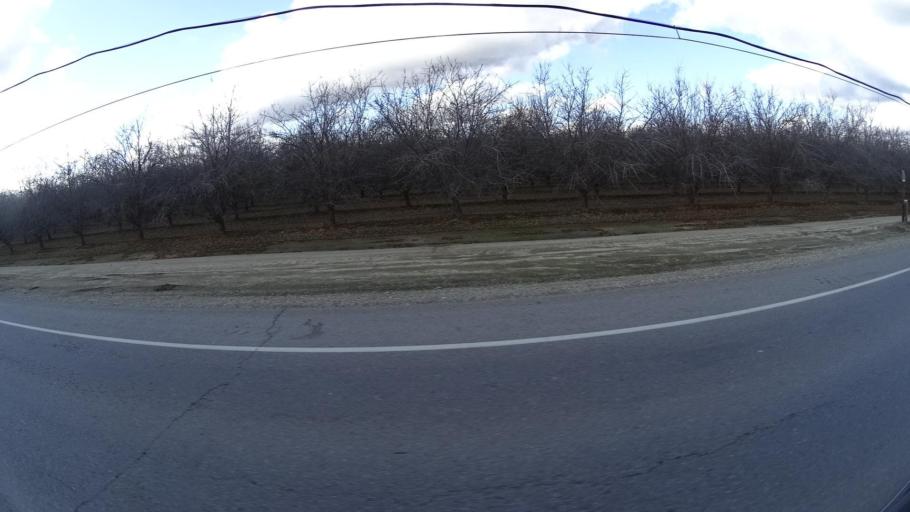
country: US
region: California
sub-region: Kern County
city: Greenfield
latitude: 35.2173
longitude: -119.1099
